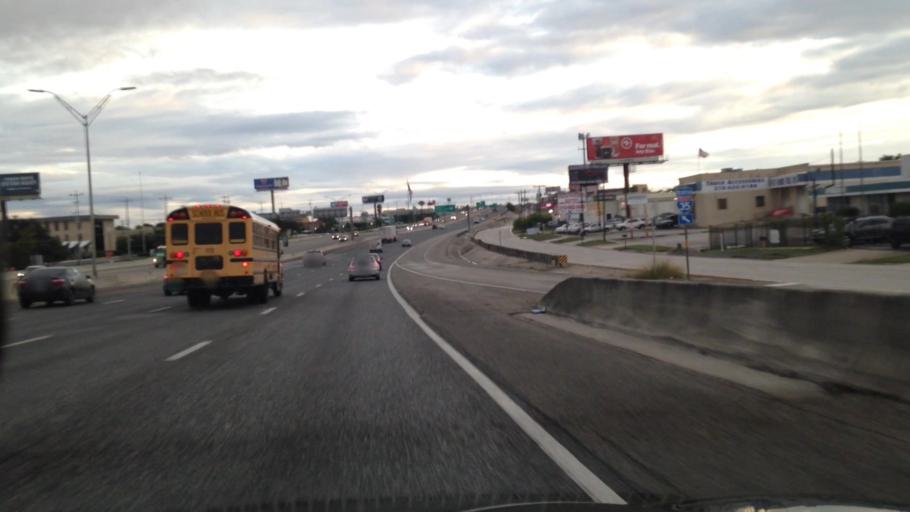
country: US
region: Texas
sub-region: Bexar County
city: Windcrest
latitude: 29.5343
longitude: -98.3881
